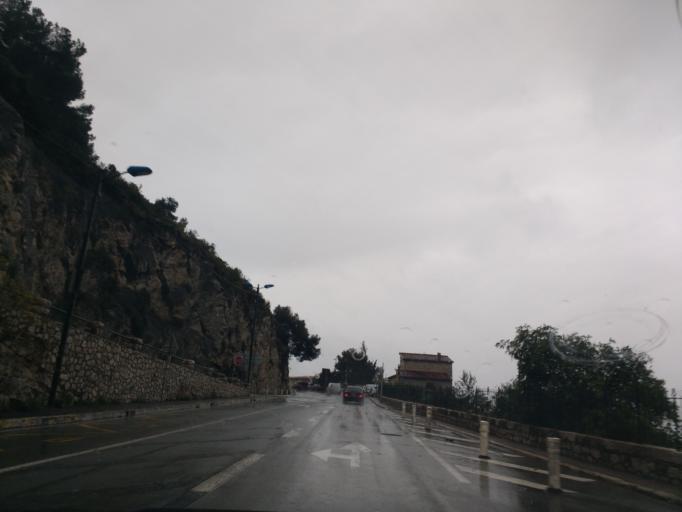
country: FR
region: Provence-Alpes-Cote d'Azur
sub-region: Departement des Alpes-Maritimes
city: Eze
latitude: 43.7245
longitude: 7.3819
